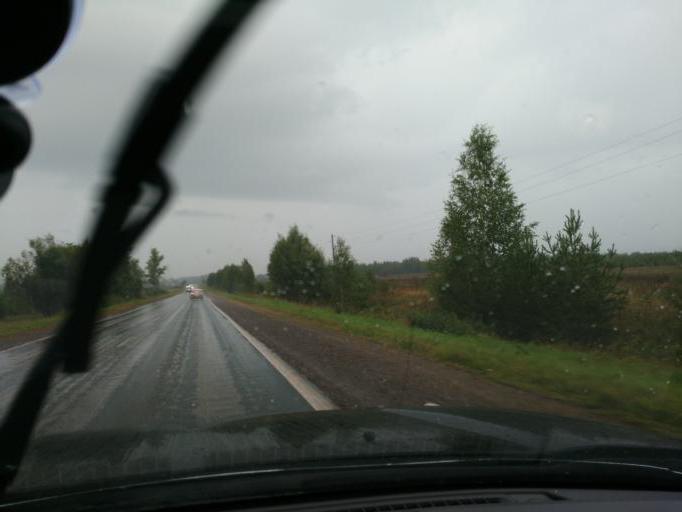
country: RU
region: Perm
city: Osa
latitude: 57.1332
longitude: 55.5264
